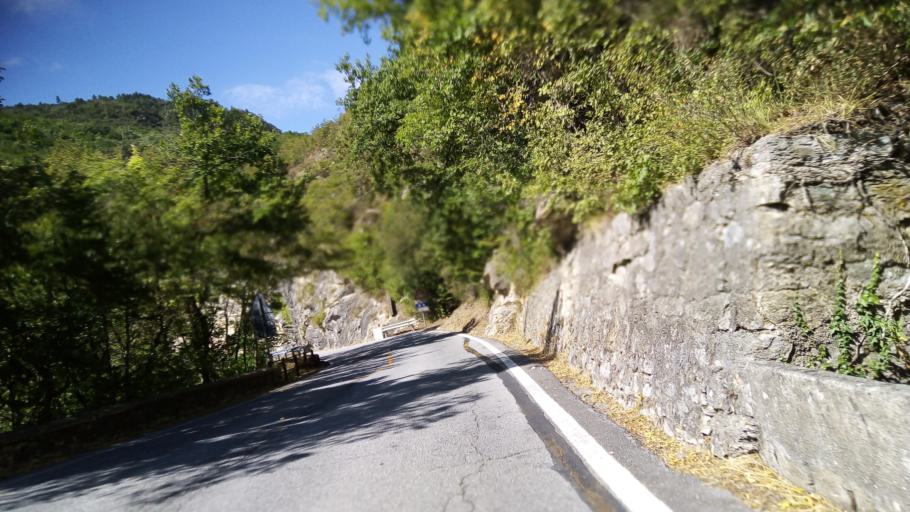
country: IT
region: Liguria
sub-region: Provincia di Savona
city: Balestrino
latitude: 44.1394
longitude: 8.1597
